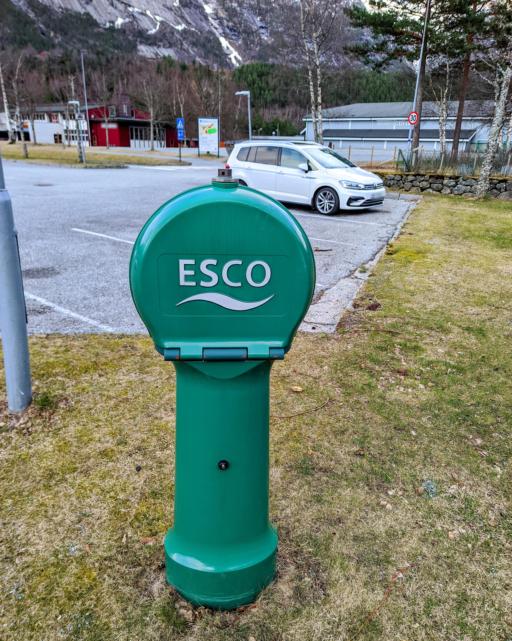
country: NO
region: Hordaland
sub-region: Eidfjord
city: Eidfjord
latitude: 60.4635
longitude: 7.0693
